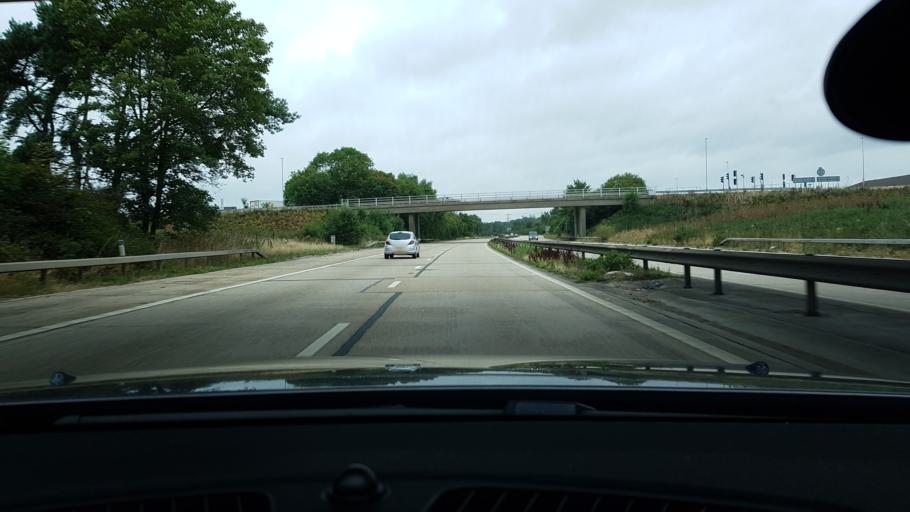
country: GB
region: England
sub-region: Hampshire
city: Totton
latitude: 50.9327
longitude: -1.4737
